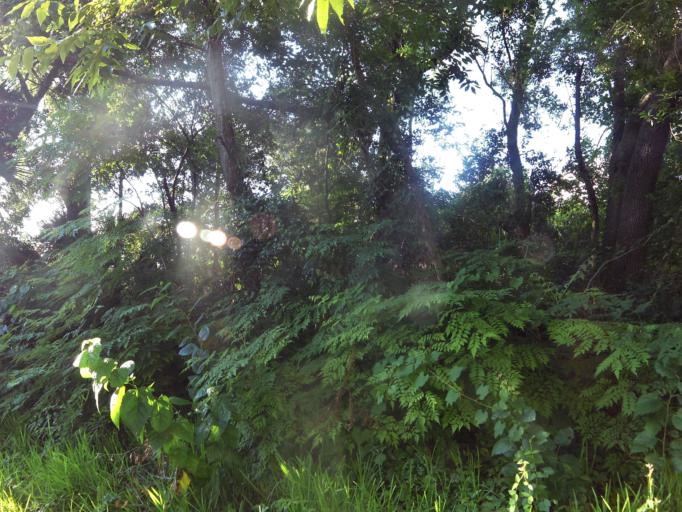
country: US
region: Florida
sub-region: Duval County
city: Jacksonville
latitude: 30.3291
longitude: -81.6890
